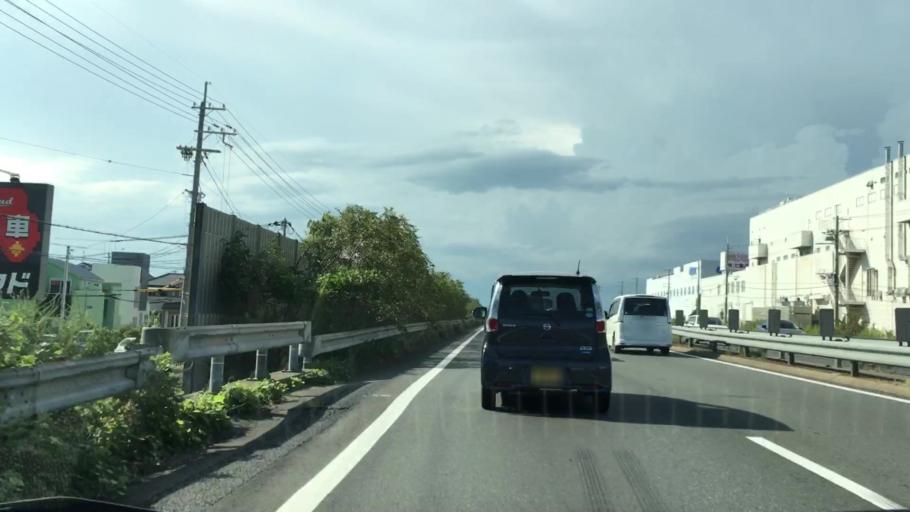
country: JP
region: Hyogo
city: Kakogawacho-honmachi
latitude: 34.7337
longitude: 134.8847
